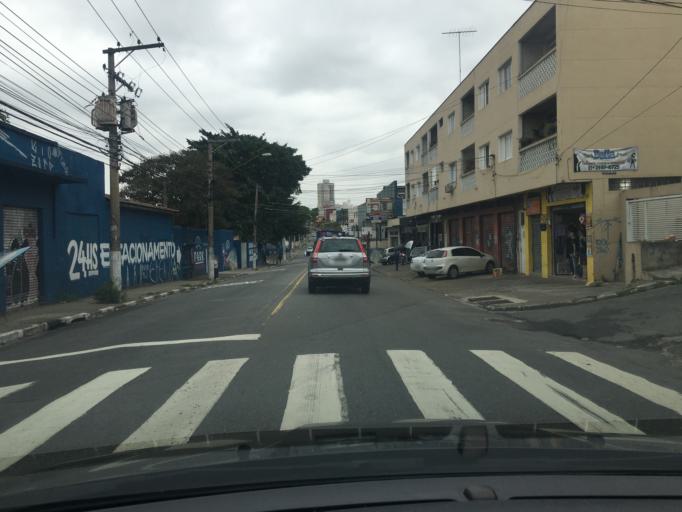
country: BR
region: Sao Paulo
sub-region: Guarulhos
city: Guarulhos
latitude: -23.4933
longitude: -46.5466
